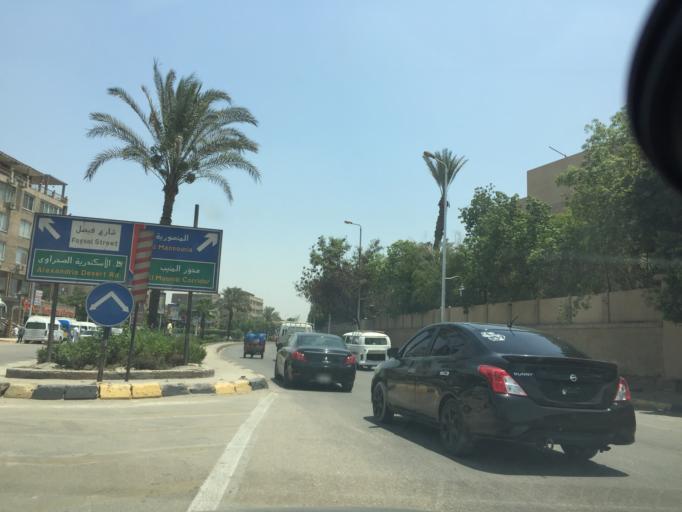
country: EG
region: Al Jizah
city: Al Jizah
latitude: 29.9871
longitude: 31.1329
